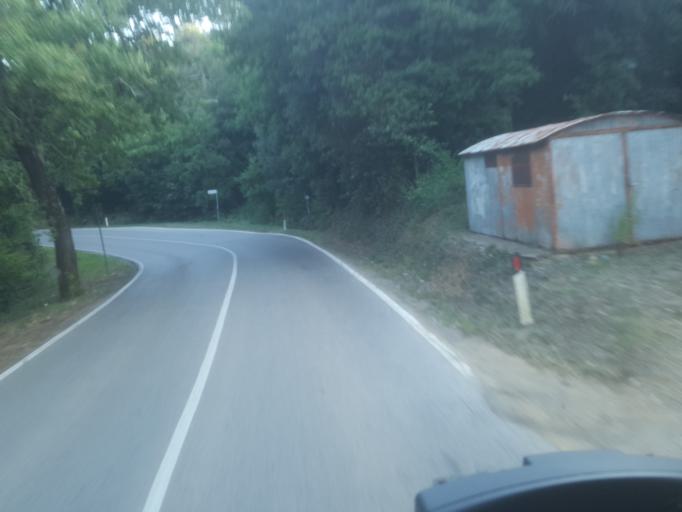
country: IT
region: Tuscany
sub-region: Province of Florence
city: Montaione
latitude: 43.5328
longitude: 10.9241
